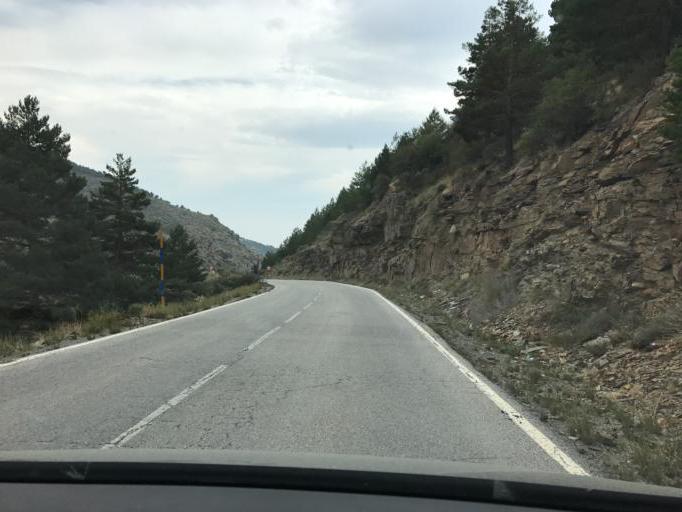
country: ES
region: Andalusia
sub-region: Provincia de Almeria
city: Bayarcal
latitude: 37.0851
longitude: -3.0244
